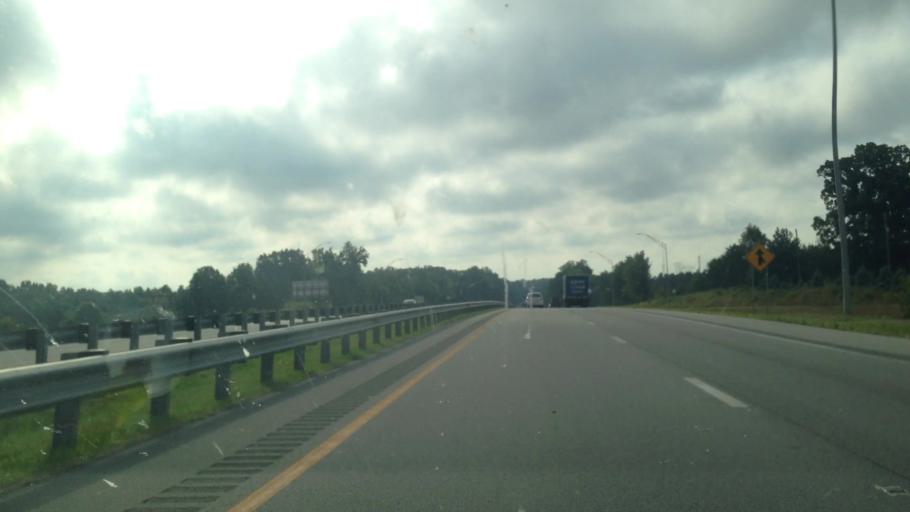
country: US
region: North Carolina
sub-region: Forsyth County
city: Kernersville
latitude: 36.1063
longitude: -80.0448
